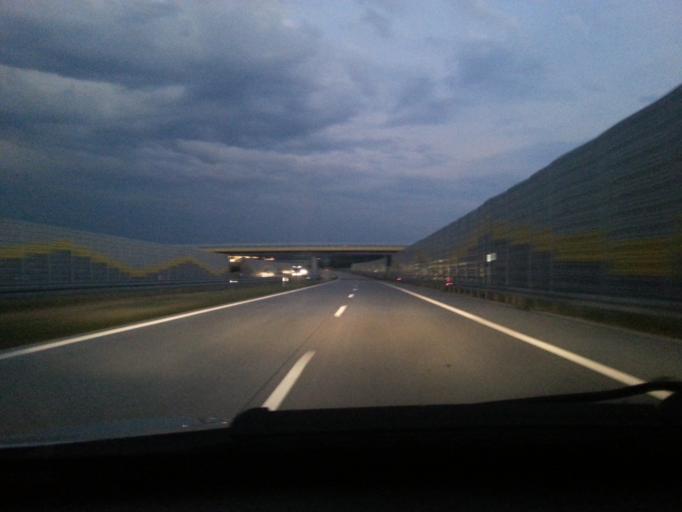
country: PL
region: Lodz Voivodeship
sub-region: Powiat sieradzki
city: Sieradz
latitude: 51.5450
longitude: 18.7009
